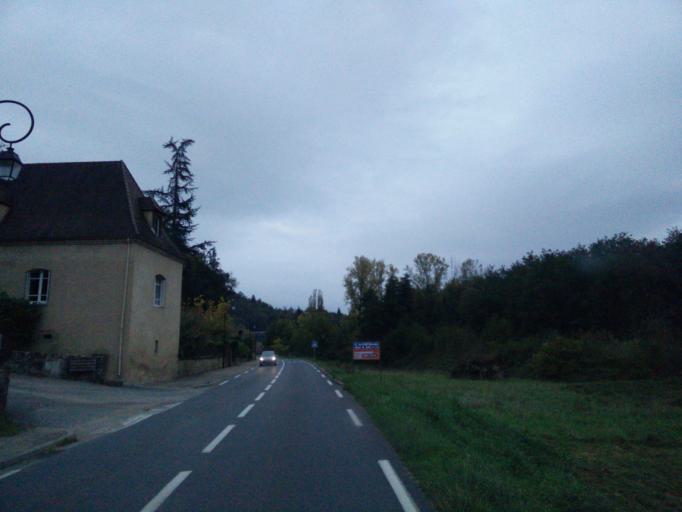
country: FR
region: Aquitaine
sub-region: Departement de la Dordogne
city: Carsac-Aillac
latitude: 44.8111
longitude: 1.2952
